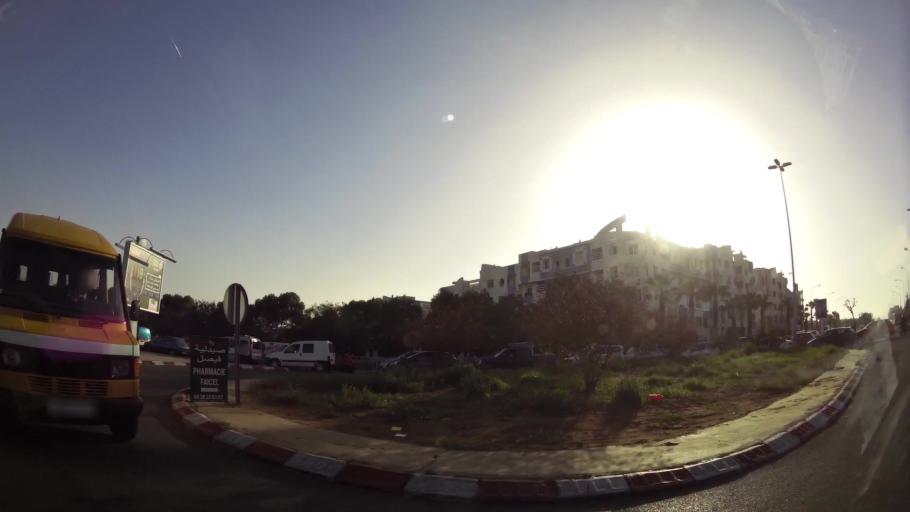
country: MA
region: Oued ed Dahab-Lagouira
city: Dakhla
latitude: 30.4056
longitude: -9.5511
